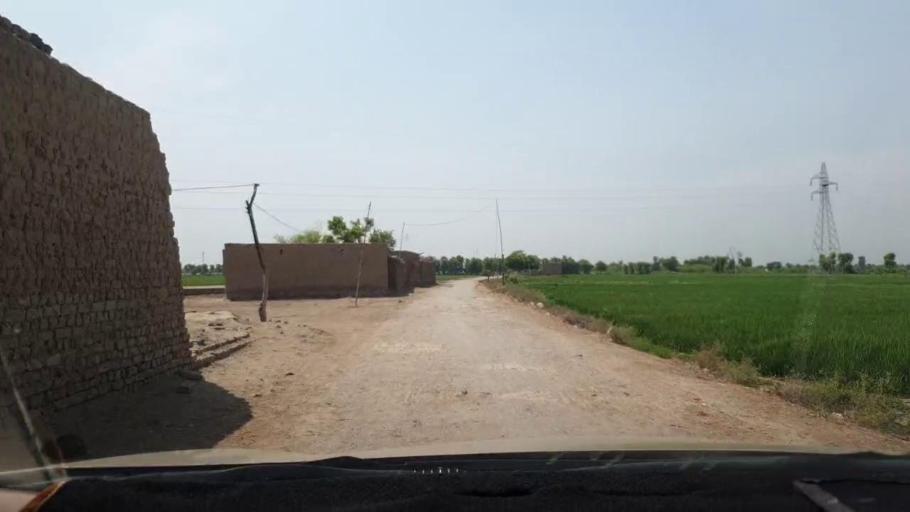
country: PK
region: Sindh
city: Naudero
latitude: 27.6306
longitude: 68.2739
